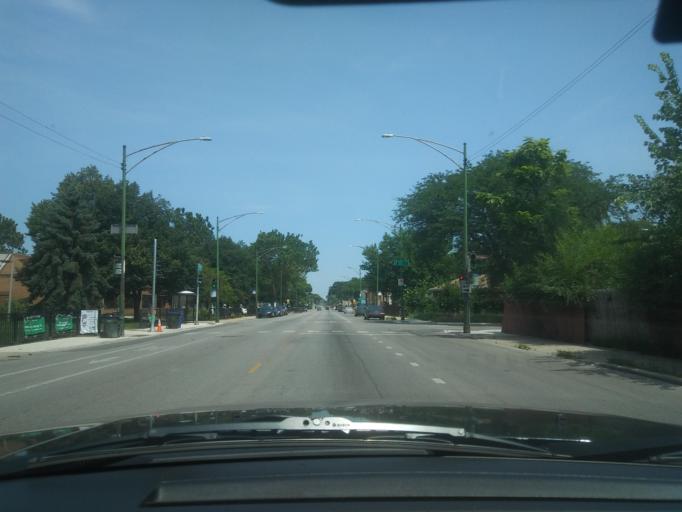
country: US
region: Illinois
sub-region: Cook County
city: Evergreen Park
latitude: 41.7827
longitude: -87.6739
